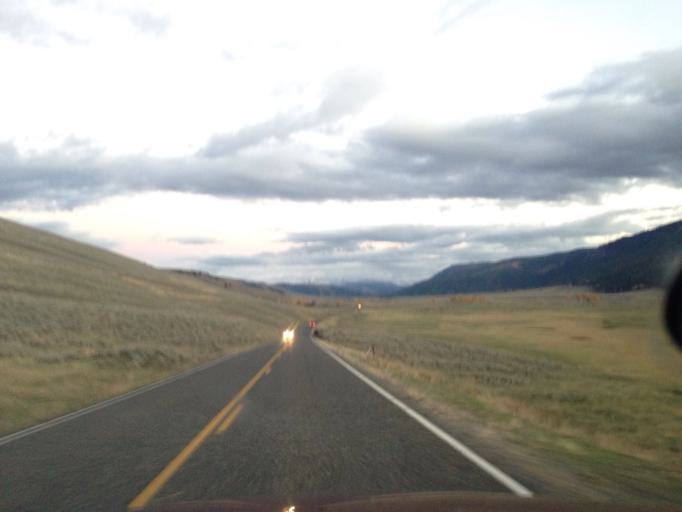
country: US
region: Montana
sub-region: Park County
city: Livingston
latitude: 44.9041
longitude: -110.2465
